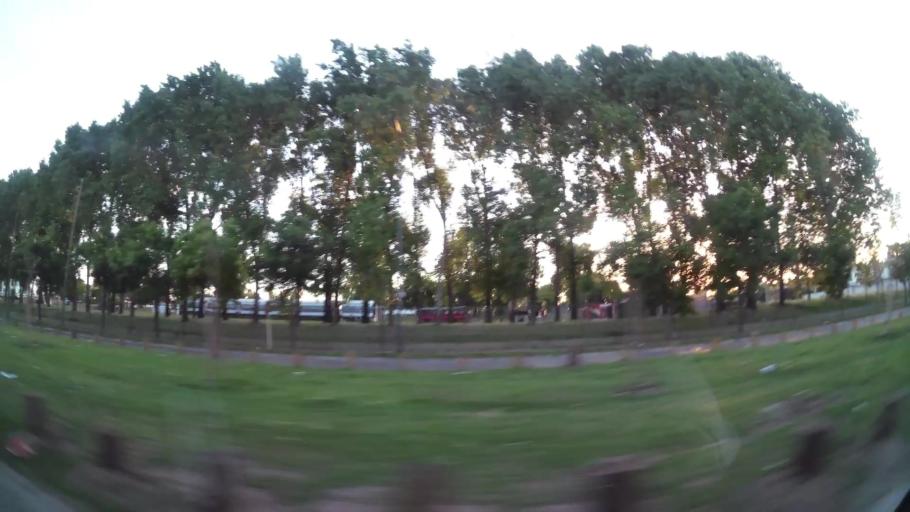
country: AR
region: Buenos Aires F.D.
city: Villa Lugano
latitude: -34.6665
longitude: -58.4675
